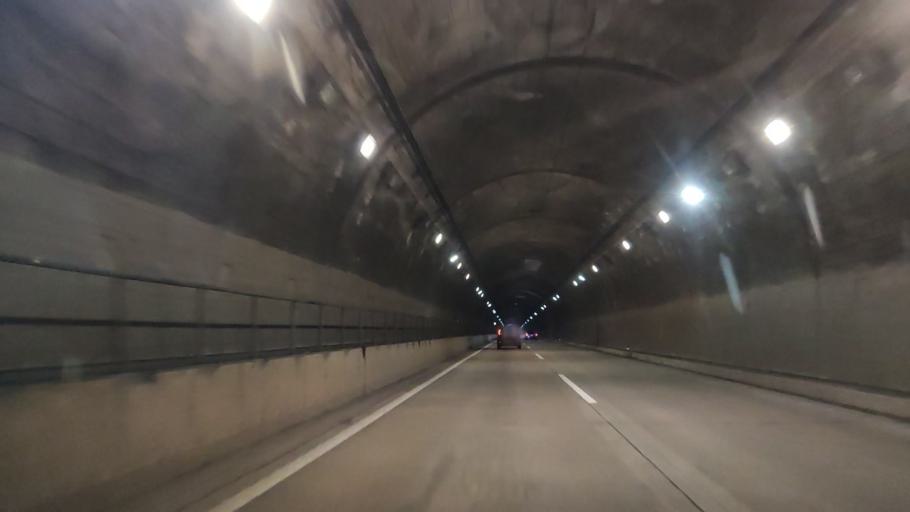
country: JP
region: Tokushima
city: Narutocho-mitsuishi
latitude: 34.1786
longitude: 134.5913
